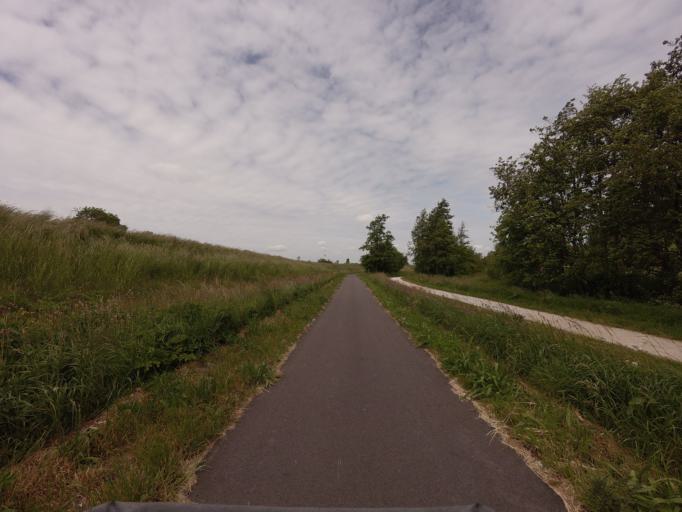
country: NL
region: North Holland
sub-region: Gemeente Medemblik
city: Medemblik
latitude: 52.7616
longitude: 5.1183
